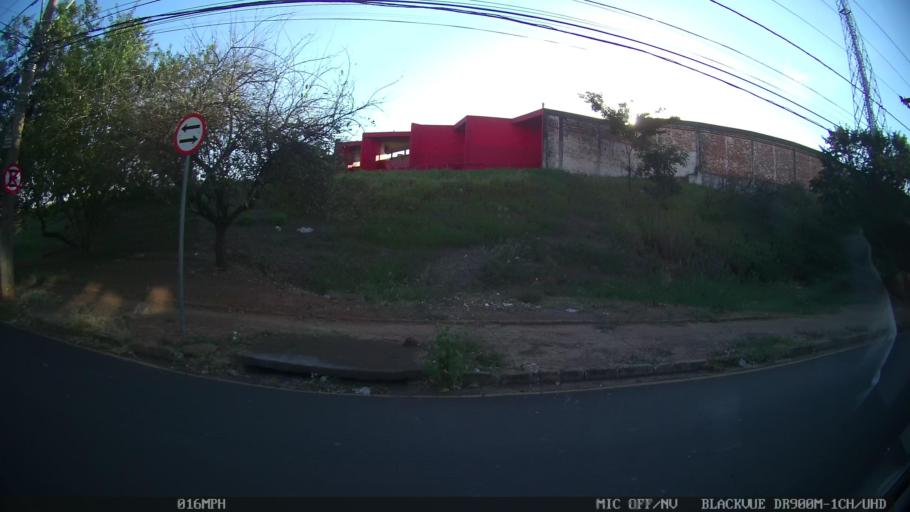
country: BR
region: Sao Paulo
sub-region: Sao Jose Do Rio Preto
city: Sao Jose do Rio Preto
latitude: -20.7978
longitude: -49.3578
